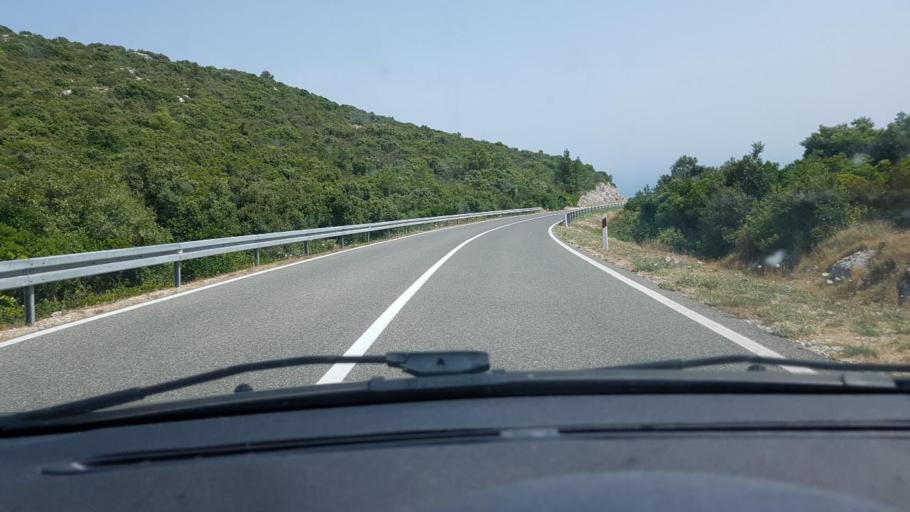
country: HR
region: Dubrovacko-Neretvanska
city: Smokvica
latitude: 42.9483
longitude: 16.9522
